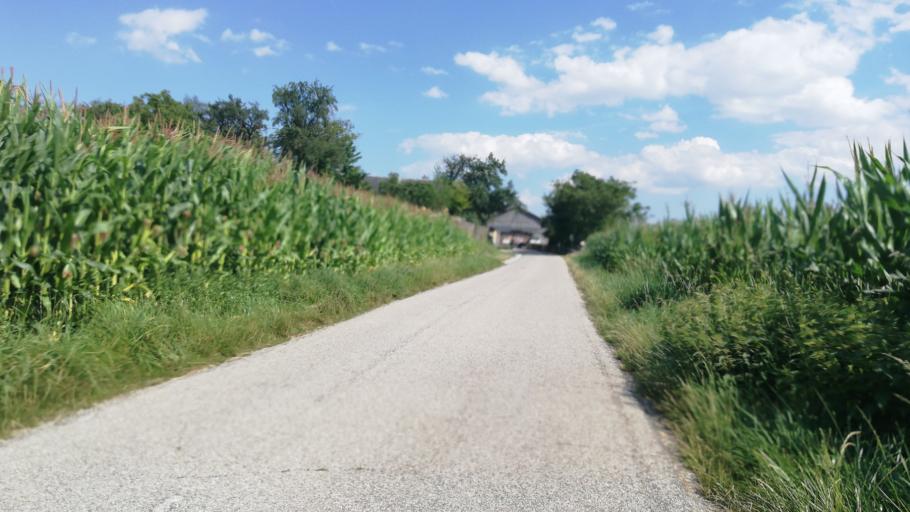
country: AT
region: Upper Austria
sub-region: Wels-Land
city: Pennewang
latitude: 48.1609
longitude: 13.8751
